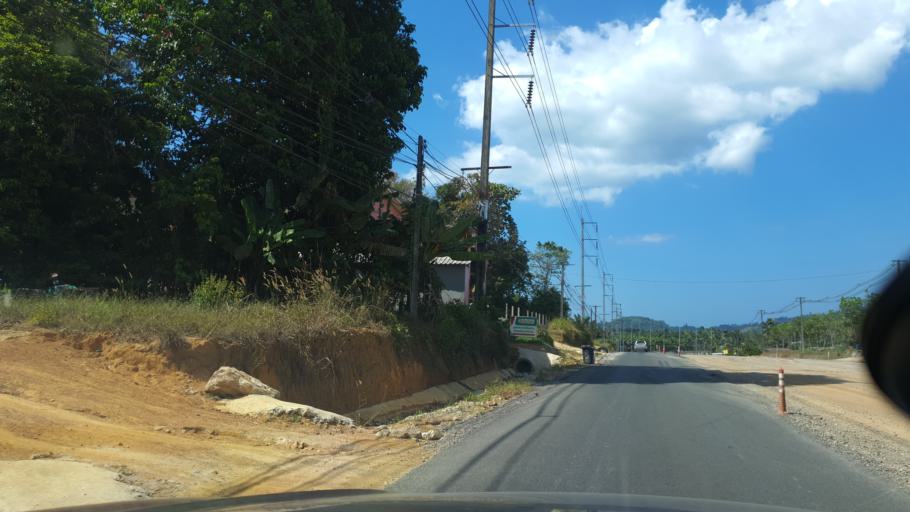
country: TH
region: Phangnga
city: Ban Khao Lak
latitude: 8.5771
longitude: 98.2621
